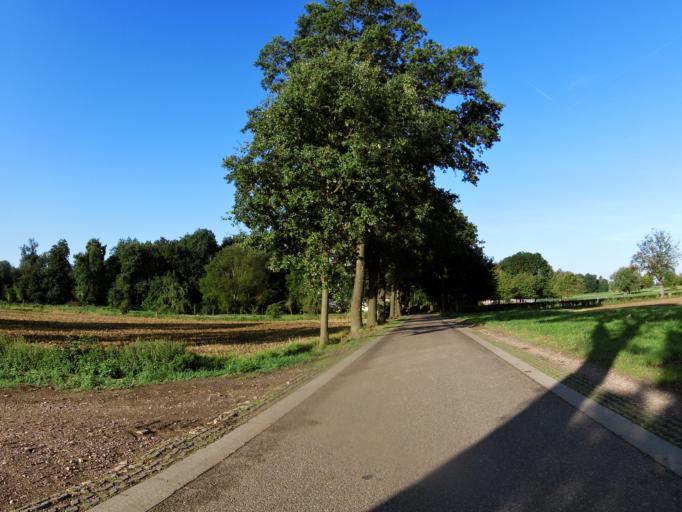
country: NL
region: Limburg
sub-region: Gemeente Voerendaal
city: Voerendaal
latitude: 50.8815
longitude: 5.9064
